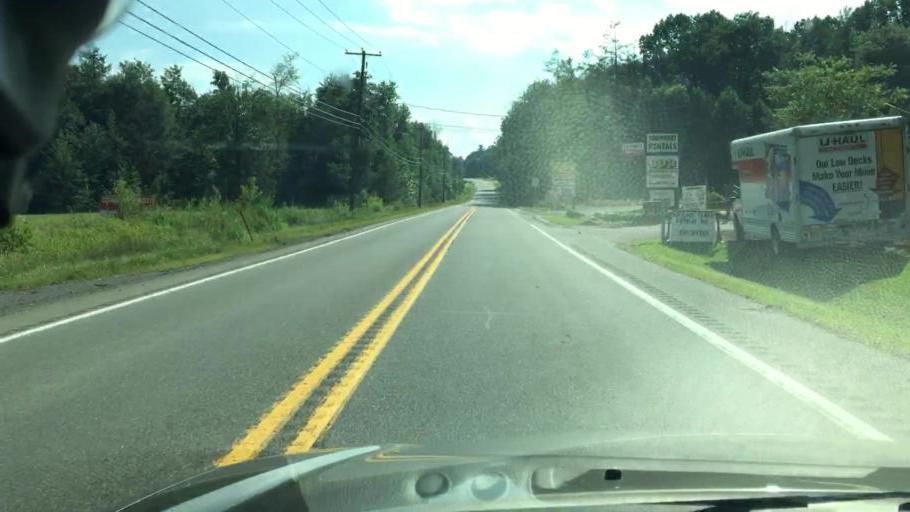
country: US
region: Pennsylvania
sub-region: Carbon County
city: Towamensing Trails
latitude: 40.9745
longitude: -75.6390
